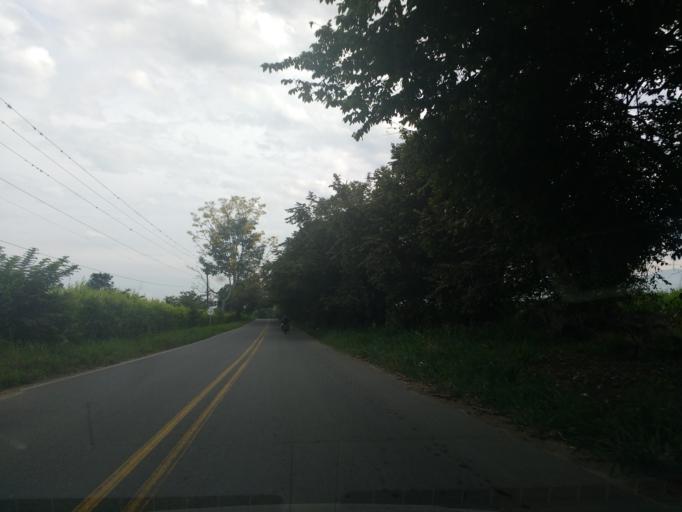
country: CO
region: Valle del Cauca
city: Florida
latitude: 3.2993
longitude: -76.2309
